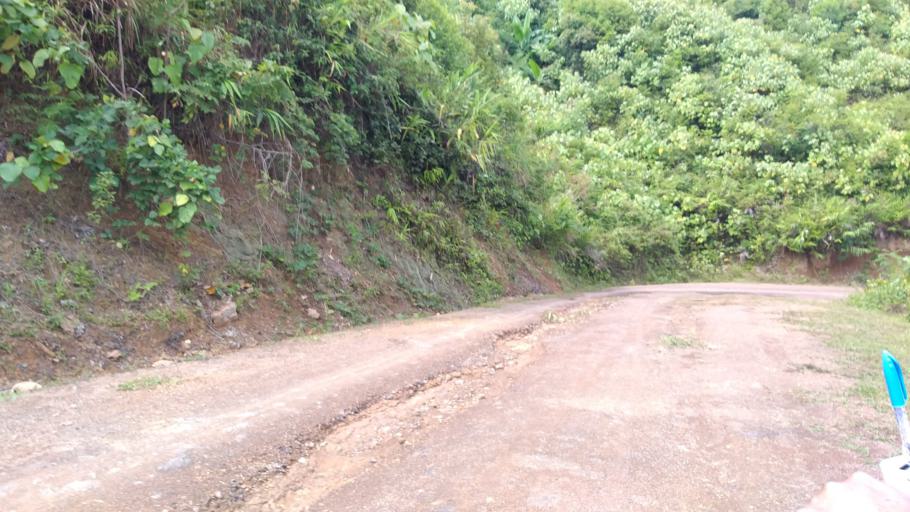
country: VN
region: Huyen Dien Bien
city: Dien Bien Phu
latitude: 21.4740
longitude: 102.6806
